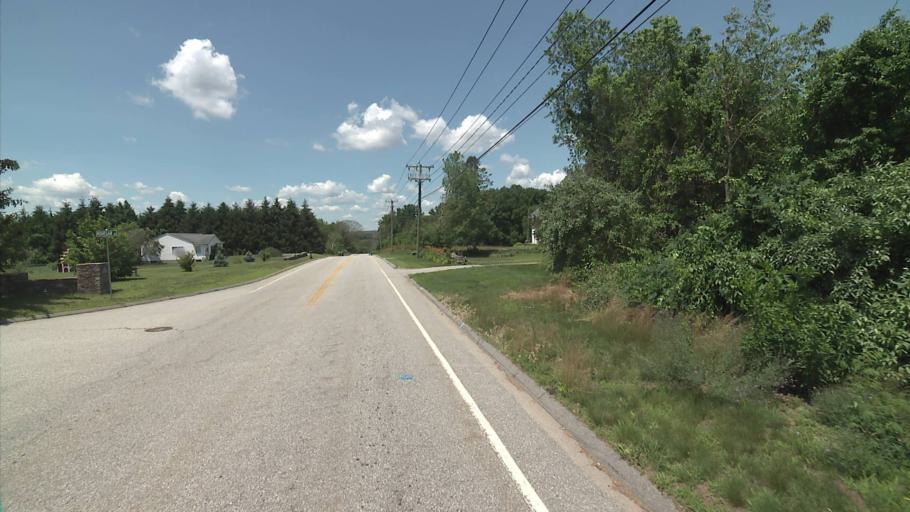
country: US
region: Connecticut
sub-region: New London County
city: Jewett City
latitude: 41.6144
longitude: -71.9555
